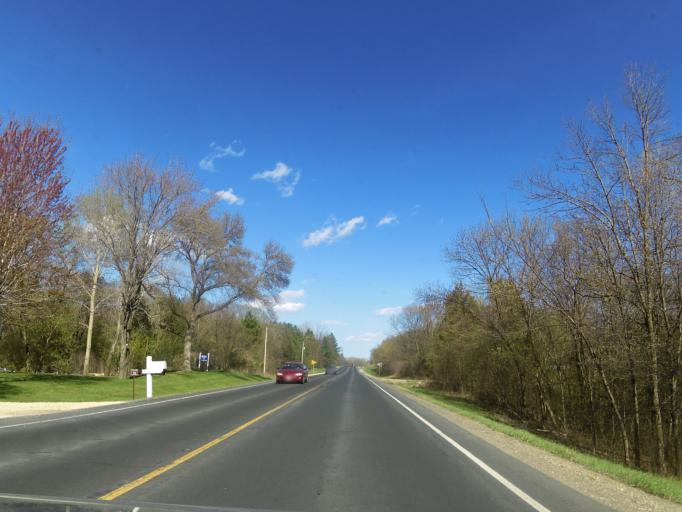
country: US
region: Minnesota
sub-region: Washington County
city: Bayport
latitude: 45.0573
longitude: -92.7372
